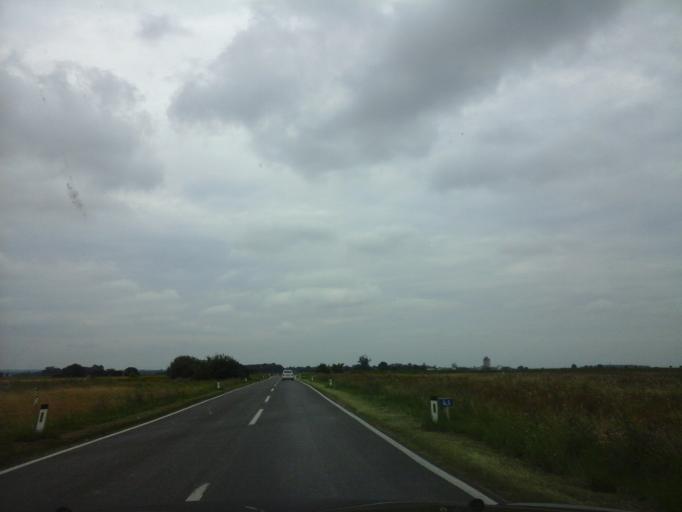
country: AT
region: Lower Austria
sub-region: Politischer Bezirk Ganserndorf
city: Eckartsau
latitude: 48.1720
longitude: 16.8336
